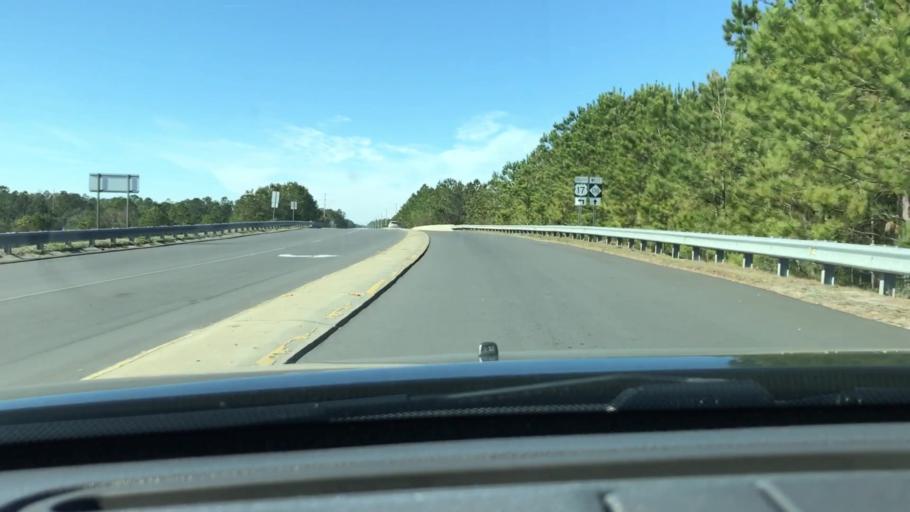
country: US
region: North Carolina
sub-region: Brunswick County
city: Shallotte
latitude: 33.9758
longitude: -78.4036
